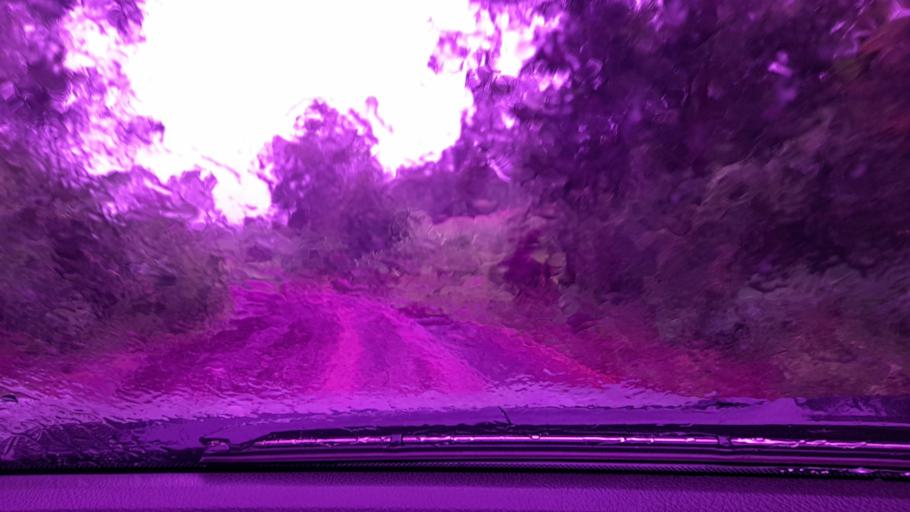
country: ET
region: Oromiya
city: Metu
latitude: 8.3543
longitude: 35.5986
